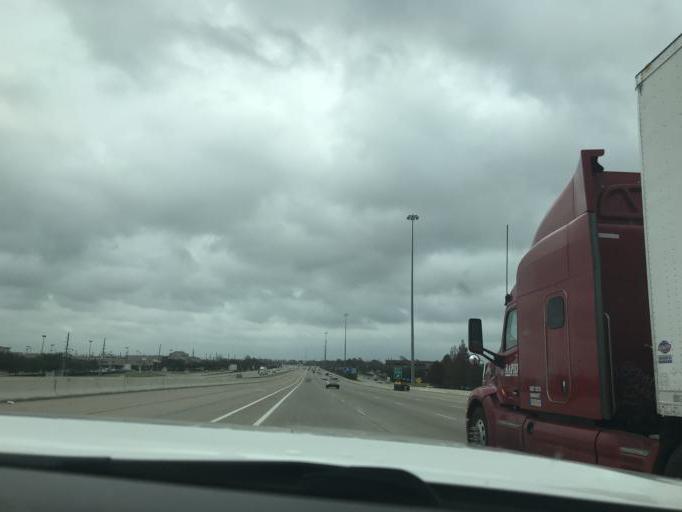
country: US
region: Texas
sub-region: Fort Bend County
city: Greatwood
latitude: 29.5619
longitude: -95.6874
